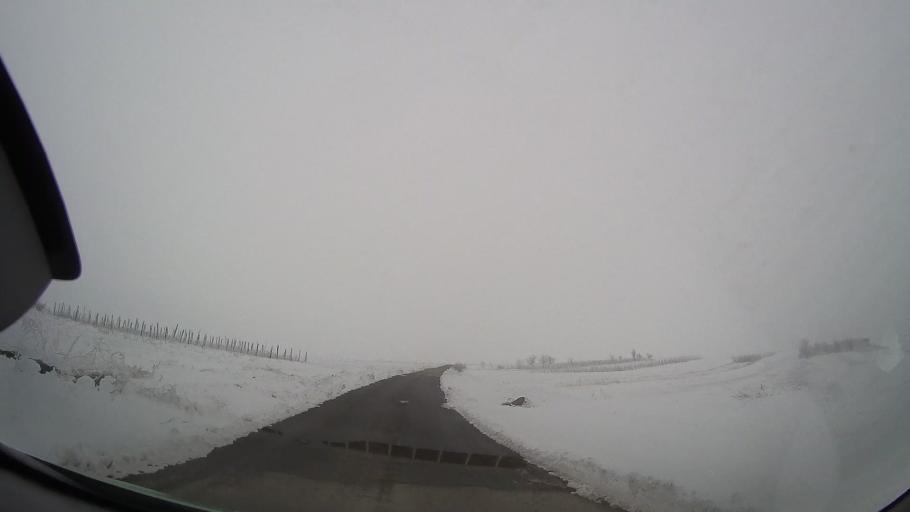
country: RO
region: Iasi
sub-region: Comuna Dagata
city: Dagata
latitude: 46.9089
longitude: 27.1972
